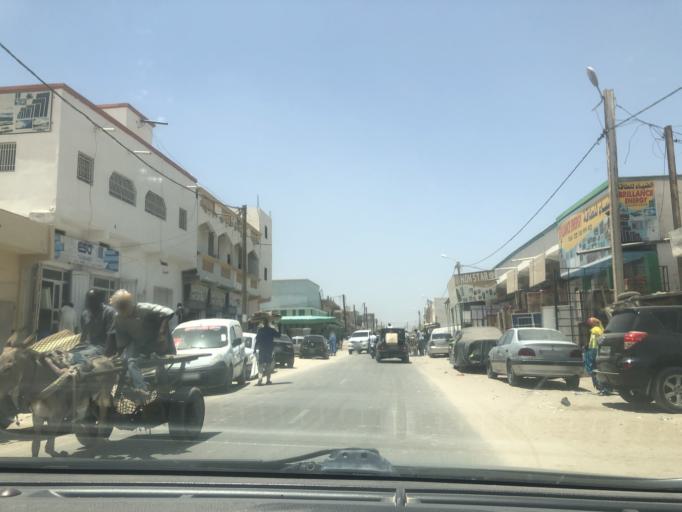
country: MR
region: Nouakchott
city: Nouakchott
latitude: 18.0737
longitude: -15.9858
